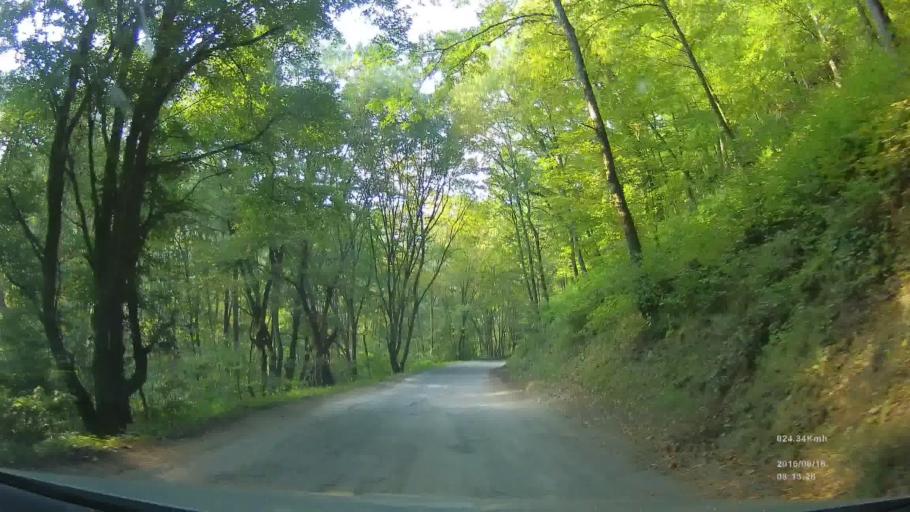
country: SK
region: Presovsky
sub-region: Okres Presov
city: Presov
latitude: 48.8753
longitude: 21.2236
